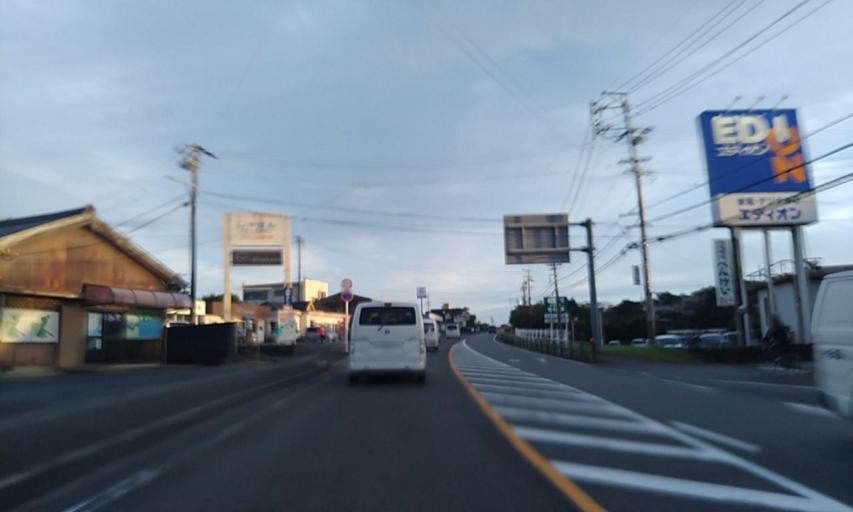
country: JP
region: Mie
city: Toba
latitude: 34.3282
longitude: 136.8395
